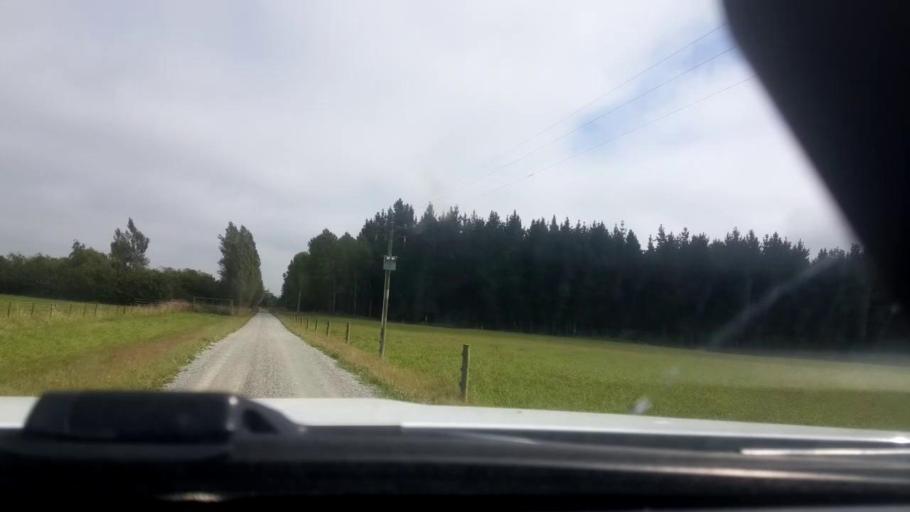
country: NZ
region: Canterbury
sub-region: Timaru District
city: Timaru
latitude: -44.3291
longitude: 171.1978
